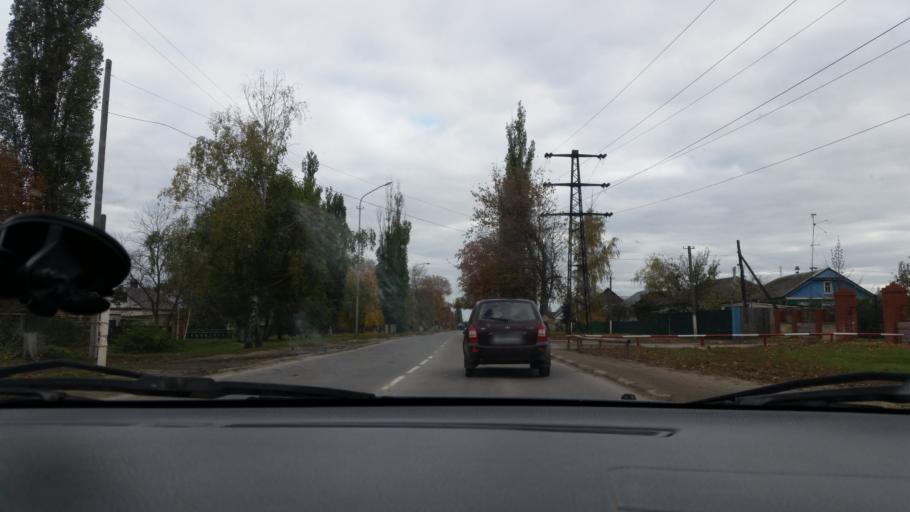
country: RU
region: Lipetsk
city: Gryazi
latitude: 52.4833
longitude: 39.9462
